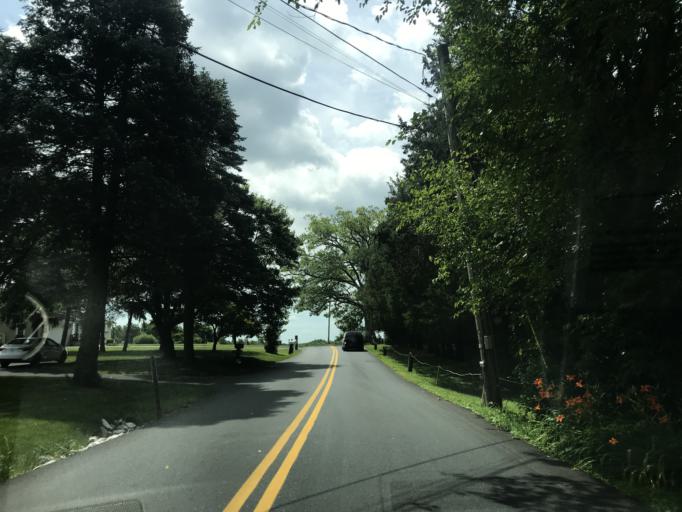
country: US
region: Maryland
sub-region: Carroll County
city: Hampstead
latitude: 39.6369
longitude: -76.8072
